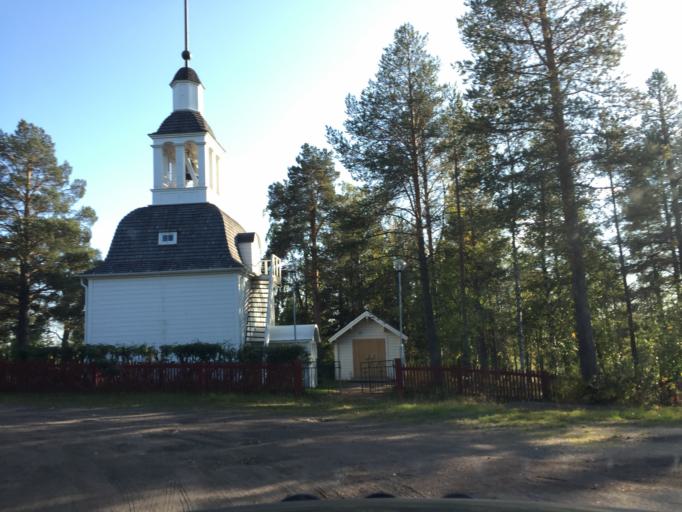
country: SE
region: Norrbotten
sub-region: Gallivare Kommun
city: Malmberget
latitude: 67.6549
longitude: 21.0312
